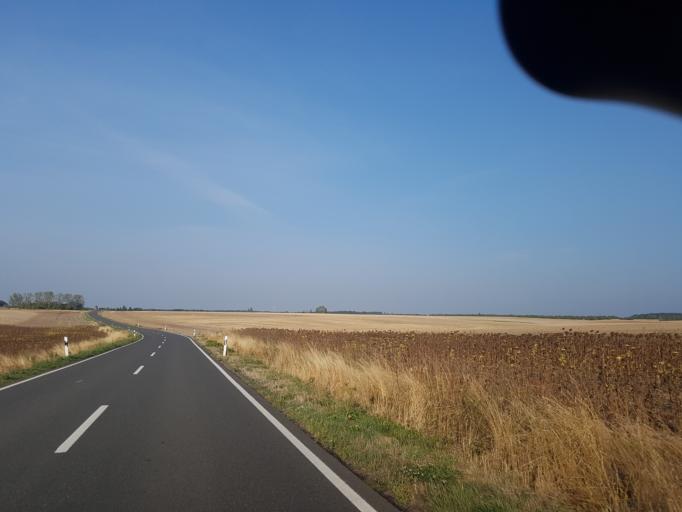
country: DE
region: Saxony-Anhalt
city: Nudersdorf
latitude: 51.9576
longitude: 12.6130
